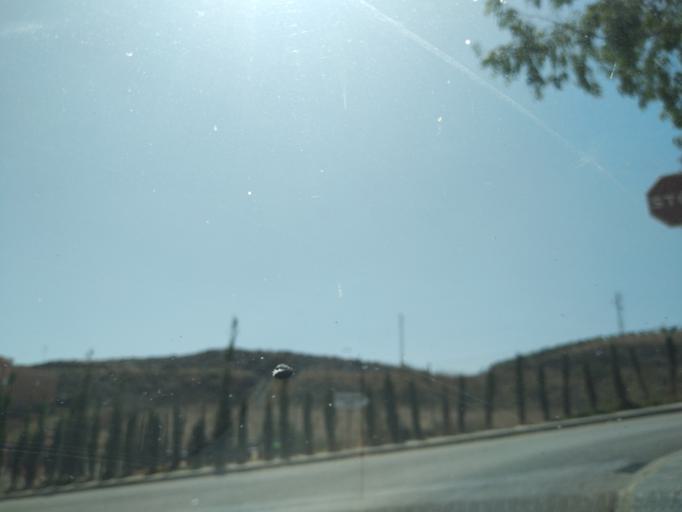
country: ES
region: Andalusia
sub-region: Provincia de Malaga
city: Valdes
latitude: 36.7215
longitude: -4.1988
